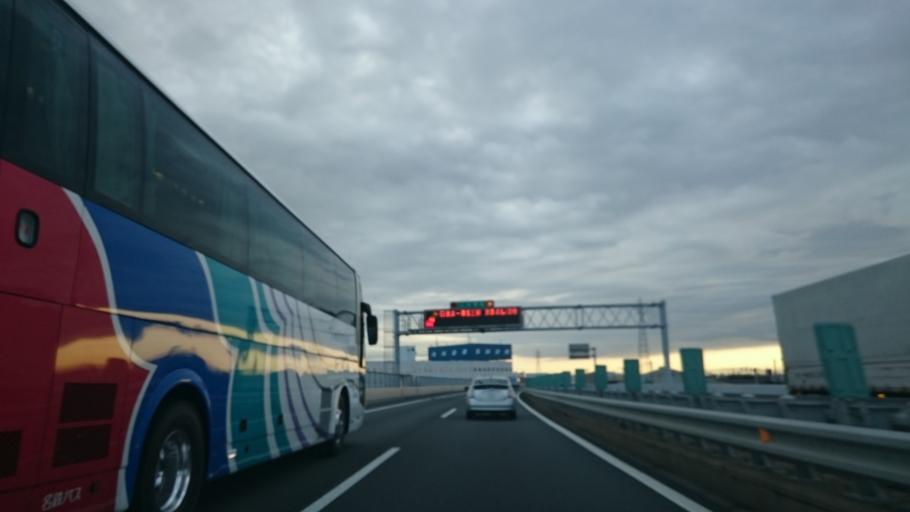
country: JP
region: Aichi
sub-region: Aisai-shi
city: Aisai
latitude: 35.1312
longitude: 136.7377
